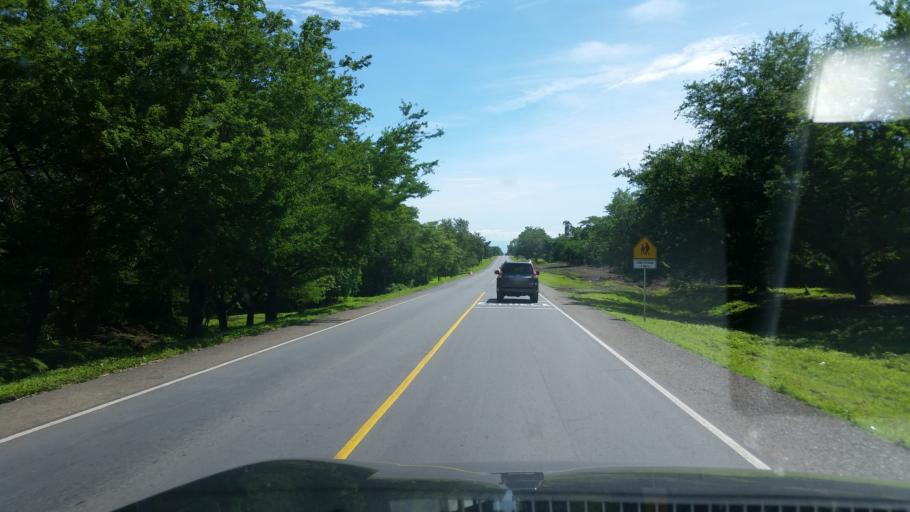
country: NI
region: Chinandega
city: El Viejo
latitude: 12.7462
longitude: -87.0704
